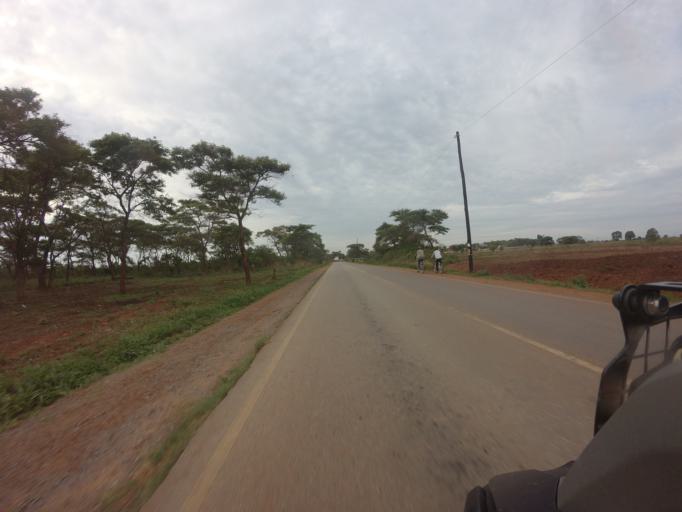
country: ZM
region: Lusaka
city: Lusaka
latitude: -15.5061
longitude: 28.2342
